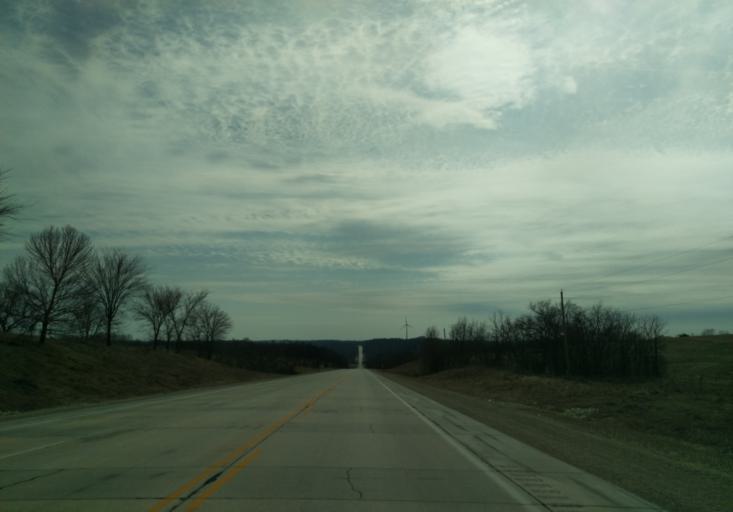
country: US
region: Iowa
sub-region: Winneshiek County
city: Decorah
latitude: 43.3330
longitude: -91.8125
